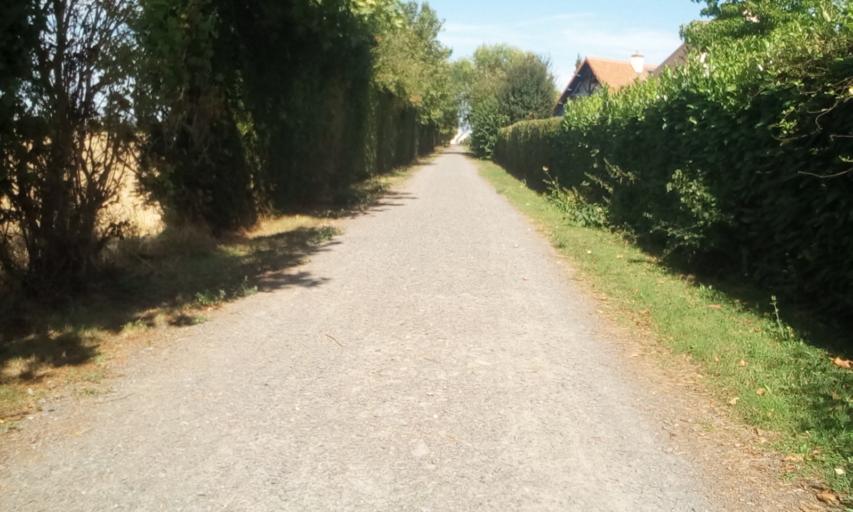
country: FR
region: Lower Normandy
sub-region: Departement du Calvados
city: Eterville
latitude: 49.1455
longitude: -0.4300
